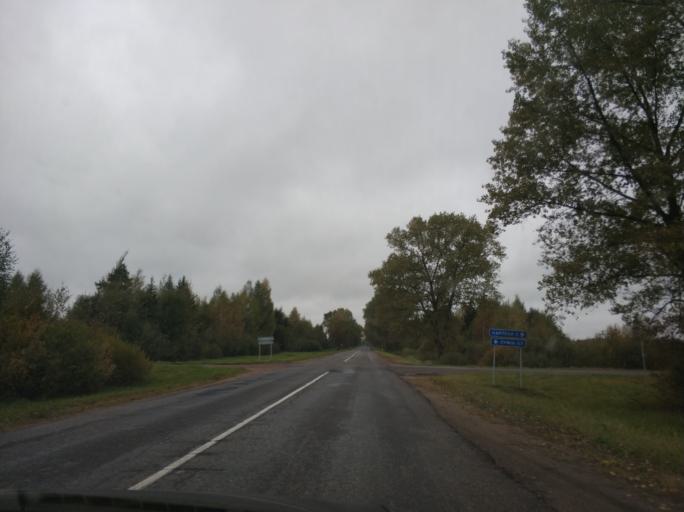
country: BY
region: Vitebsk
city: Polatsk
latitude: 55.4374
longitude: 28.9689
